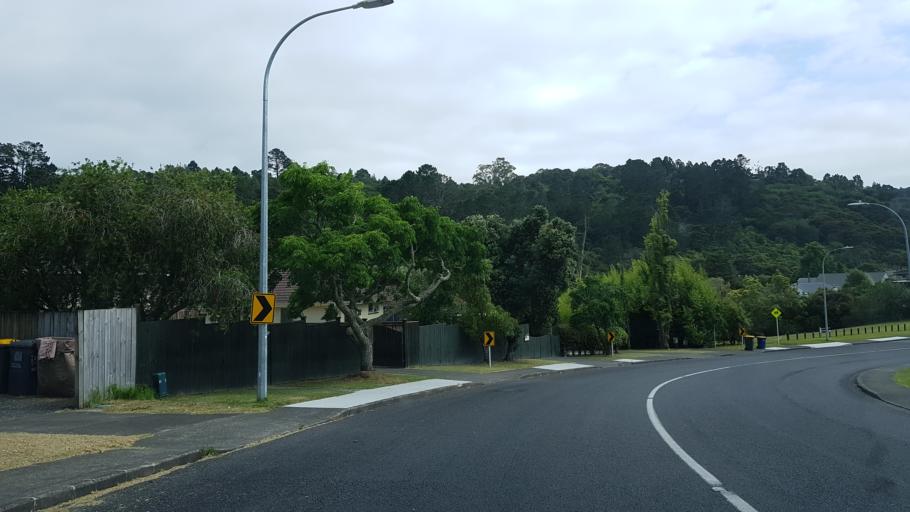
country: NZ
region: Auckland
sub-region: Auckland
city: North Shore
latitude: -36.7740
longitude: 174.7023
